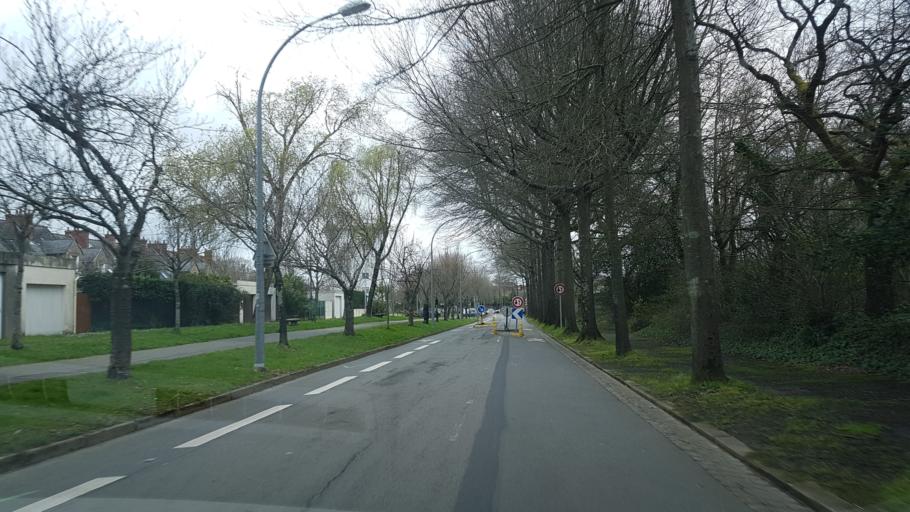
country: FR
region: Pays de la Loire
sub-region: Departement de la Loire-Atlantique
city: Nantes
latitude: 47.2456
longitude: -1.5284
